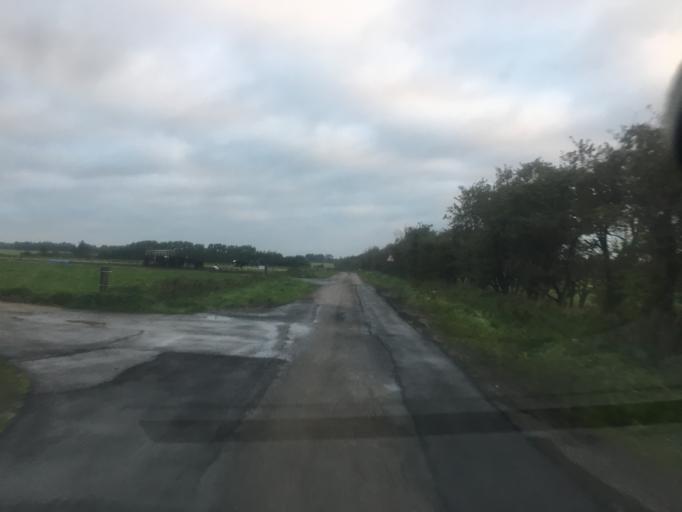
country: DK
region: South Denmark
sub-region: Tonder Kommune
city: Logumkloster
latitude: 54.9875
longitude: 8.9321
